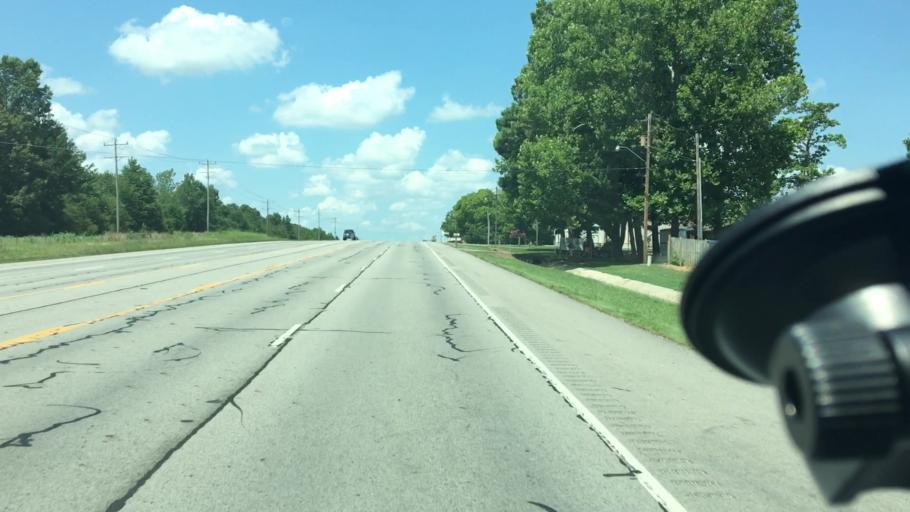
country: US
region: Arkansas
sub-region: Sebastian County
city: Barling
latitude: 35.3202
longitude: -94.2387
